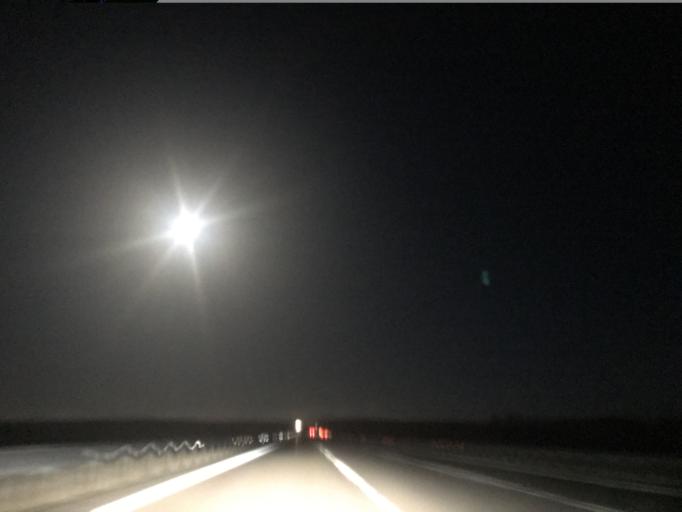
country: TR
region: Nigde
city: Ulukisla
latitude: 37.6387
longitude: 34.3928
